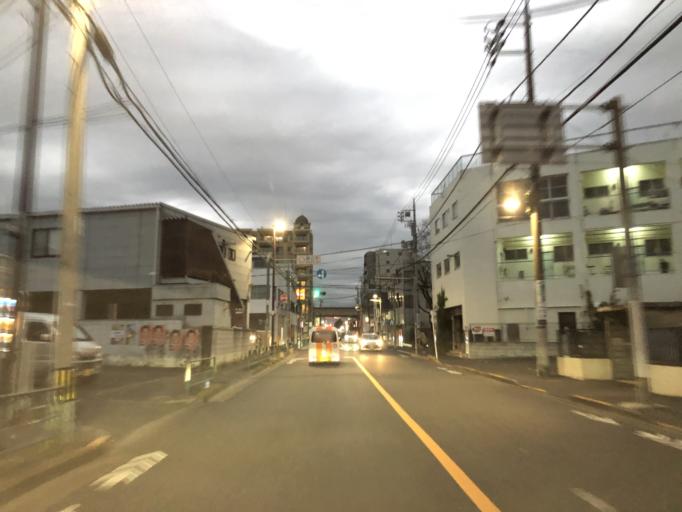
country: JP
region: Tokyo
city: Hino
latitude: 35.6972
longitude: 139.4295
